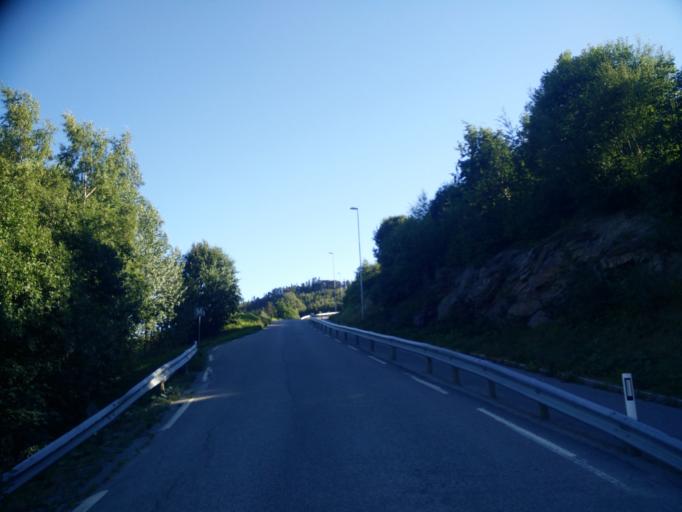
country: NO
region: Sor-Trondelag
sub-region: Skaun
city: Borsa
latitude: 63.3240
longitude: 10.0447
